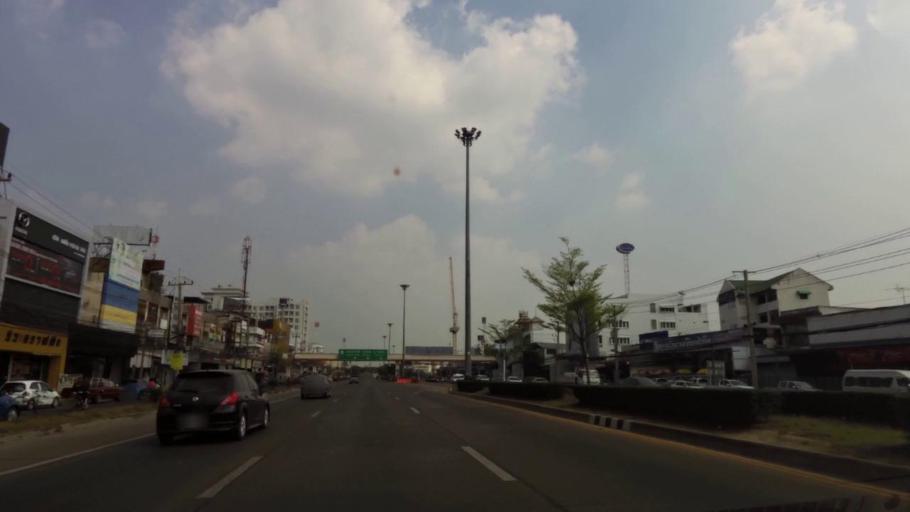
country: TH
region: Phra Nakhon Si Ayutthaya
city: Phra Nakhon Si Ayutthaya
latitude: 14.3545
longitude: 100.5950
